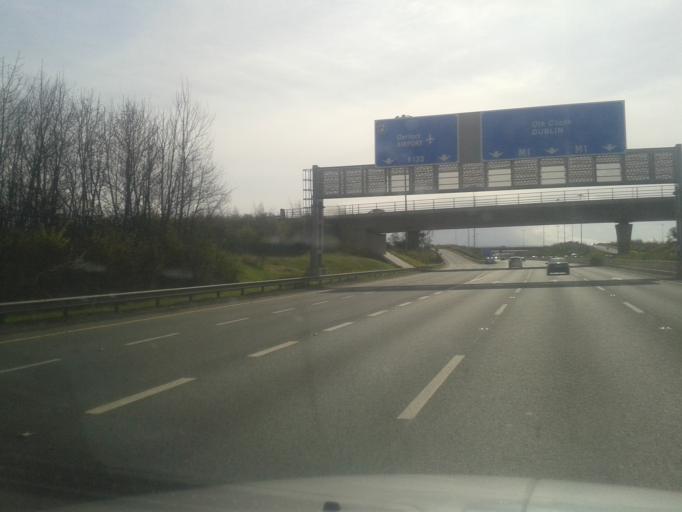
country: IE
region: Leinster
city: Kinsealy-Drinan
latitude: 53.4323
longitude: -6.2139
